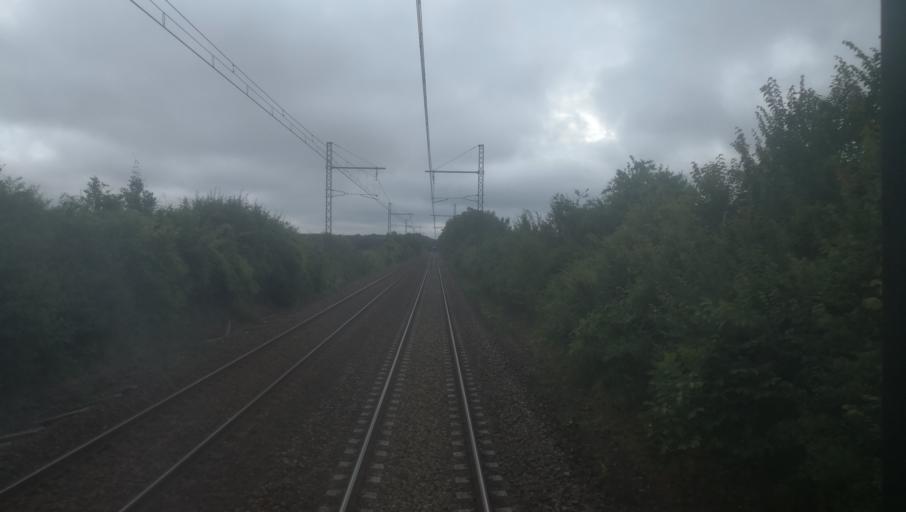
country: FR
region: Centre
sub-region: Departement de l'Indre
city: Montierchaume
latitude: 46.8365
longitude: 1.7622
